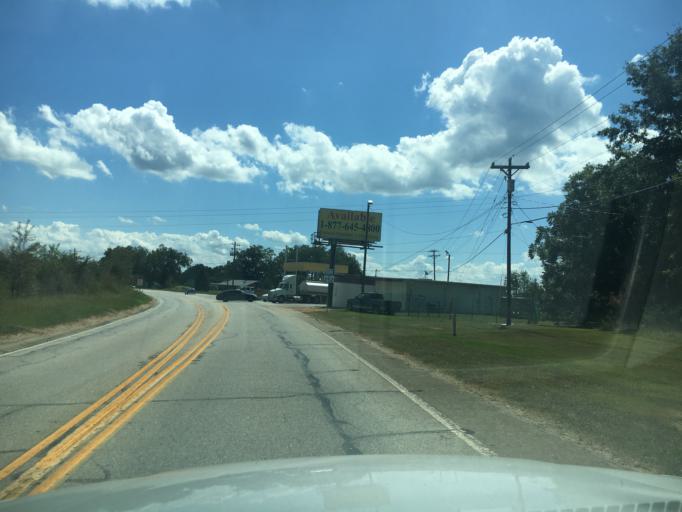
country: US
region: South Carolina
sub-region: Laurens County
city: Laurens
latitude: 34.5014
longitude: -82.0720
